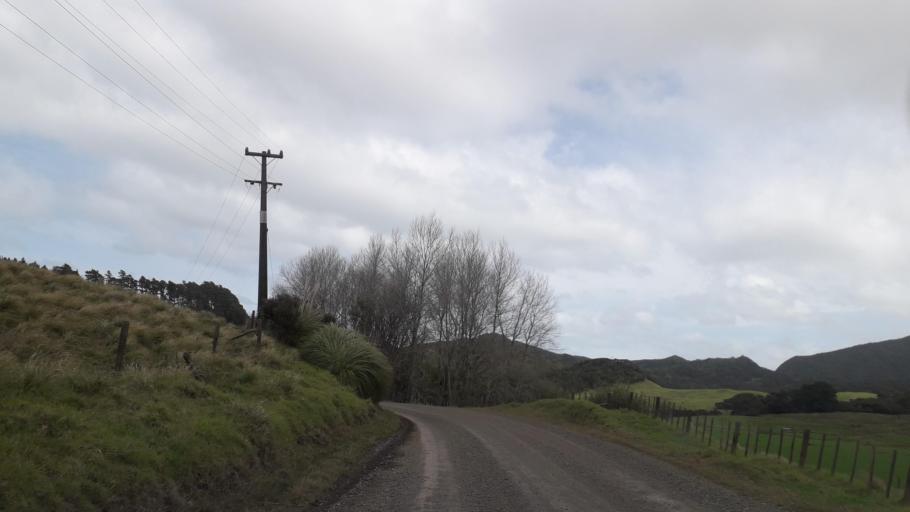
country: NZ
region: Northland
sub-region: Far North District
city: Ahipara
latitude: -35.4377
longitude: 173.3291
